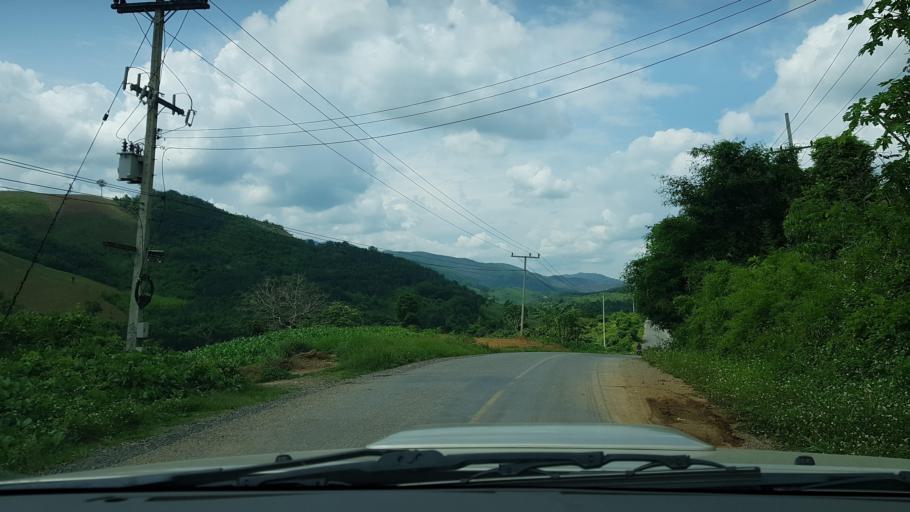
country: LA
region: Loungnamtha
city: Muang Nale
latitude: 20.1729
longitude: 101.5122
